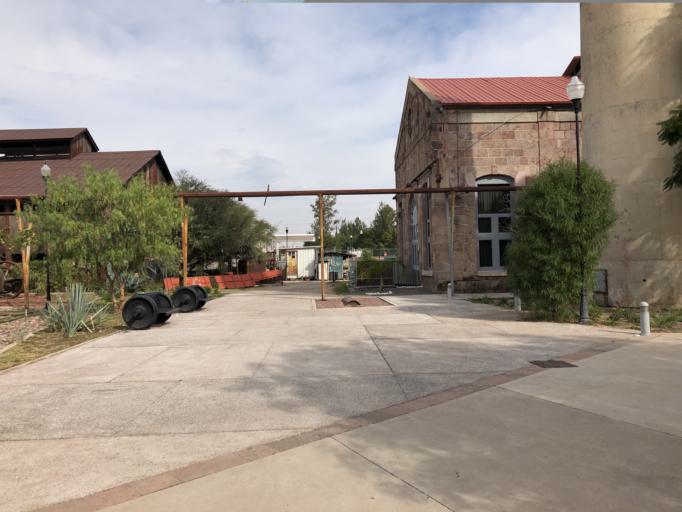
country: MX
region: Aguascalientes
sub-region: Aguascalientes
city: Aguascalientes
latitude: 21.8890
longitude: -102.2800
